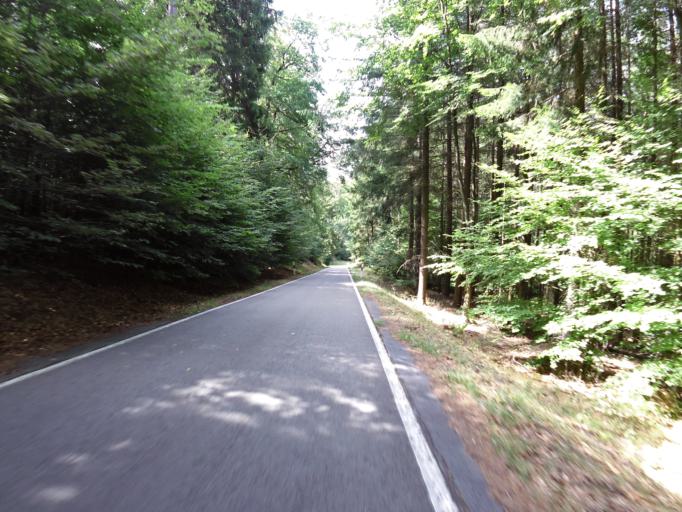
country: DE
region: Rheinland-Pfalz
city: Elmstein
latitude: 49.3862
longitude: 7.9398
